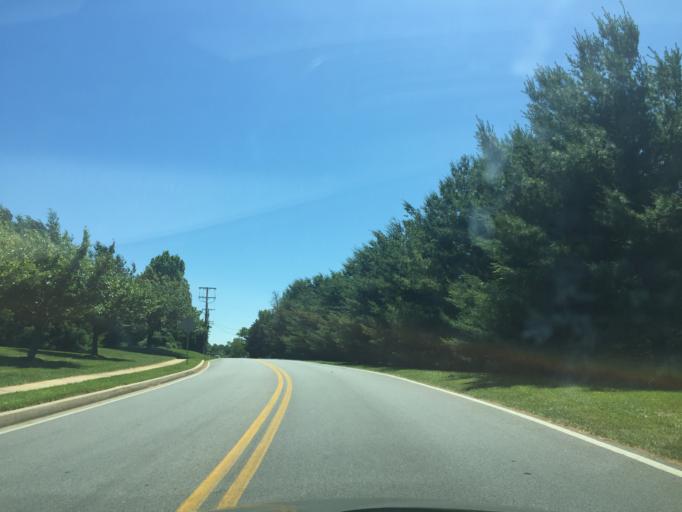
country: US
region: Maryland
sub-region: Carroll County
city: Westminster
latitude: 39.5790
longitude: -76.9787
